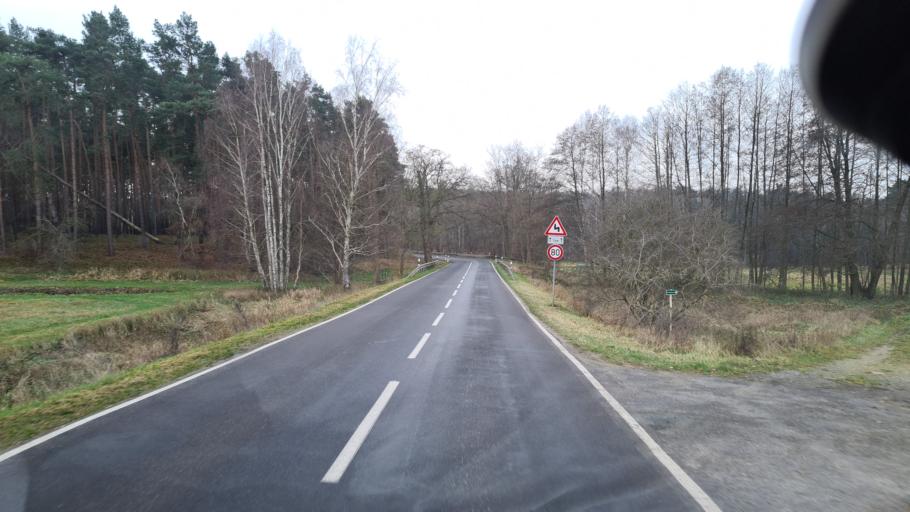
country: DE
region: Brandenburg
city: Schenkendobern
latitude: 51.9730
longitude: 14.6270
